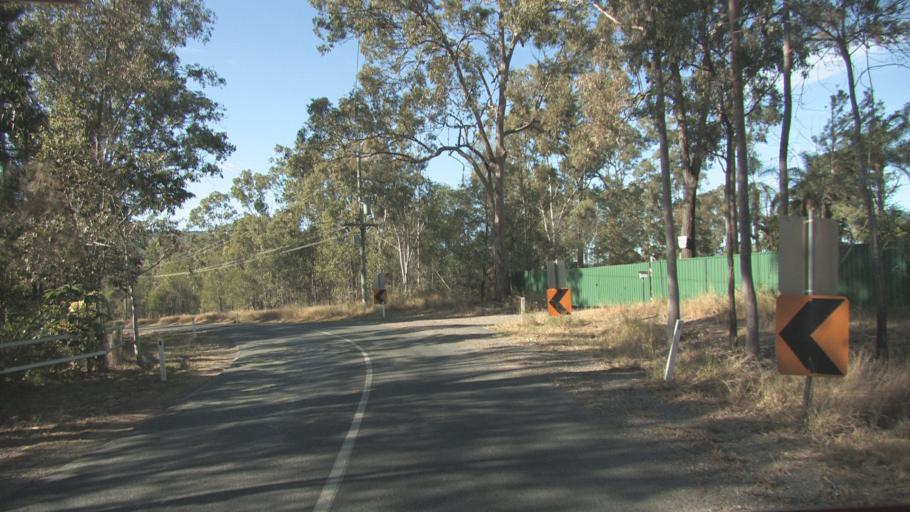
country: AU
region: Queensland
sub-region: Gold Coast
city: Ormeau Hills
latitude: -27.8235
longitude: 153.1717
